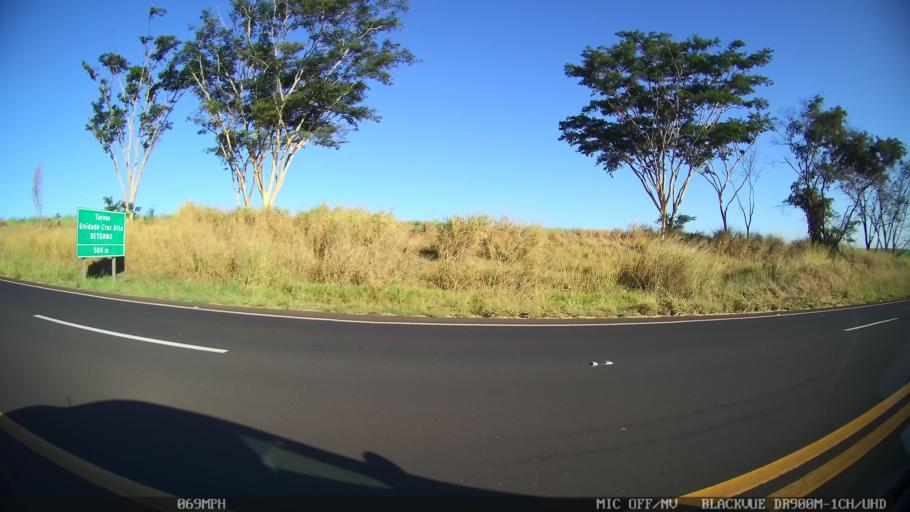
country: BR
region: Sao Paulo
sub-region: Guapiacu
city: Guapiacu
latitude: -20.7397
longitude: -49.0916
